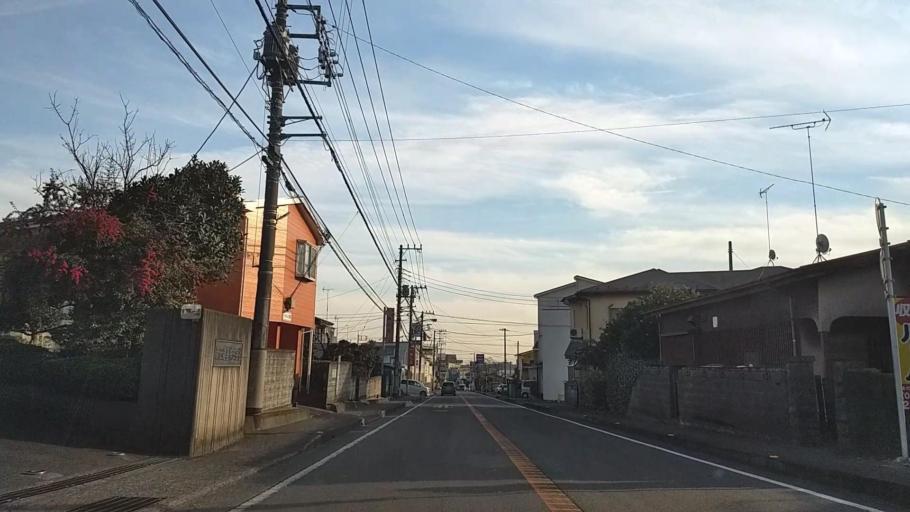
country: JP
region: Kanagawa
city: Atsugi
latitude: 35.4985
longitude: 139.3141
